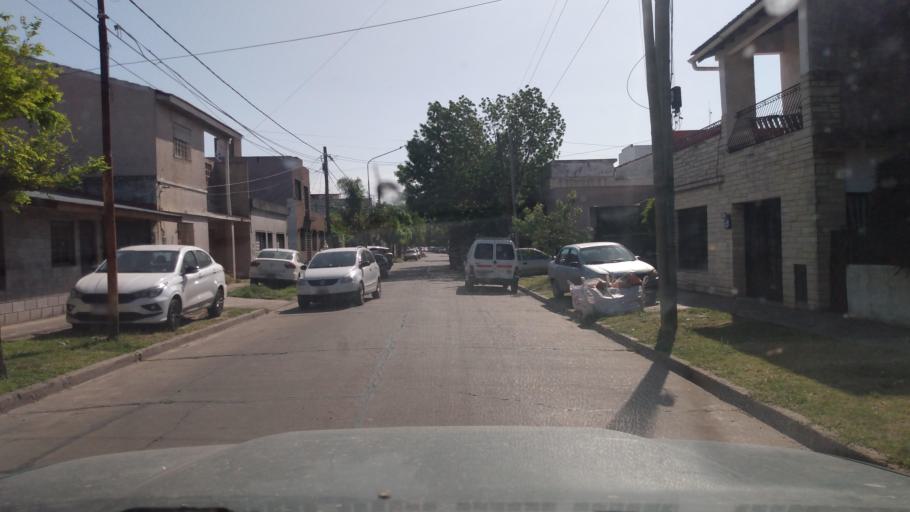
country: AR
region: Buenos Aires
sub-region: Partido de Moron
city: Moron
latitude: -34.6518
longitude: -58.5964
